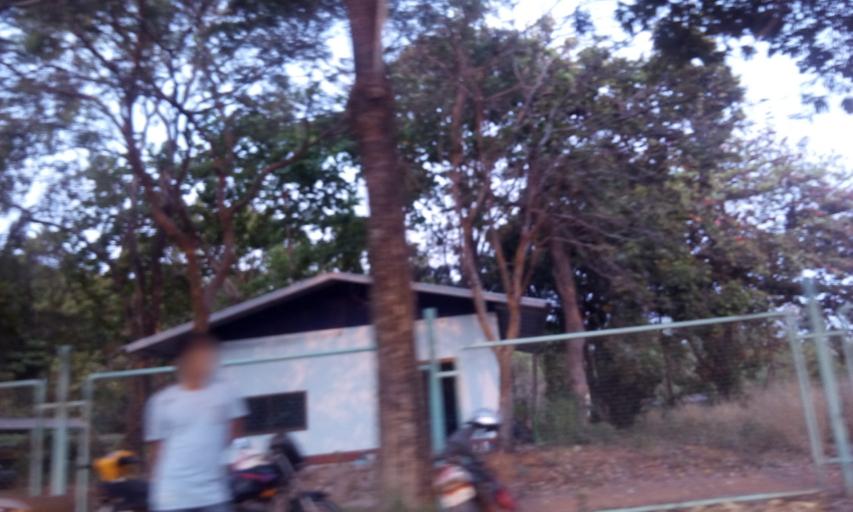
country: TH
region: Trat
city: Laem Ngop
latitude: 12.1879
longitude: 102.3015
